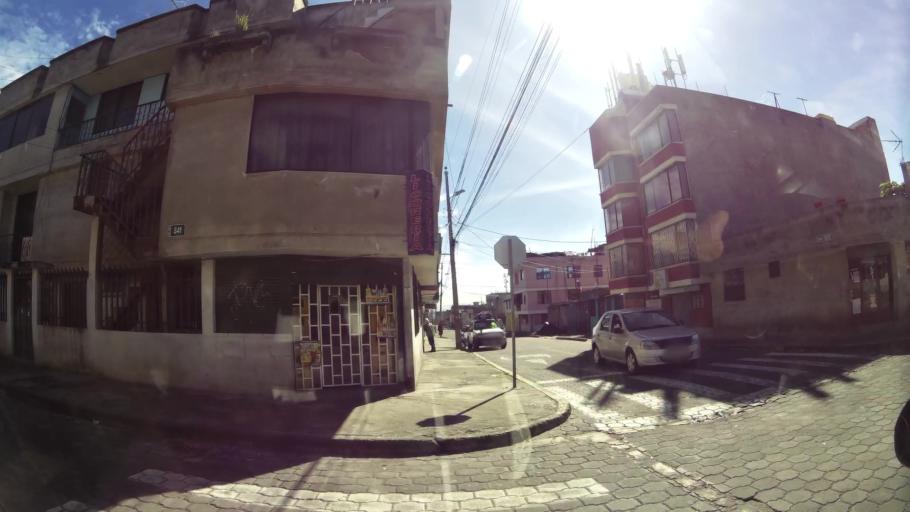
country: EC
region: Pichincha
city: Quito
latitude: -0.2988
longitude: -78.5667
